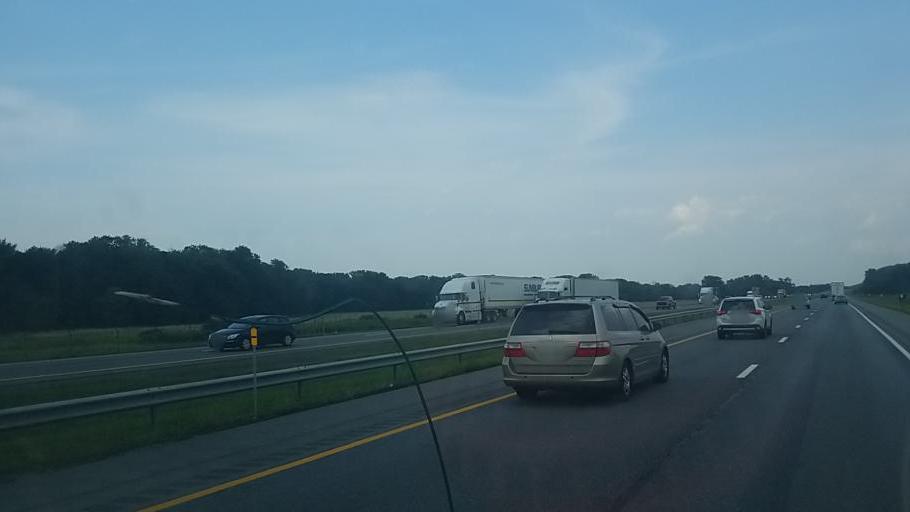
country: US
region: New York
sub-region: Seneca County
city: Bridgeport
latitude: 42.9932
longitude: -76.7481
